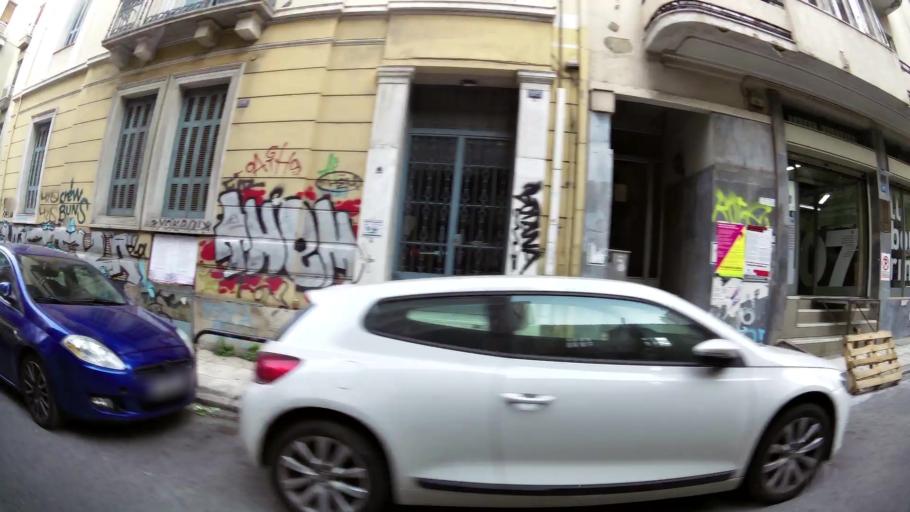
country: GR
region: Attica
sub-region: Nomarchia Athinas
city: Kipseli
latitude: 37.9864
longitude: 23.7401
